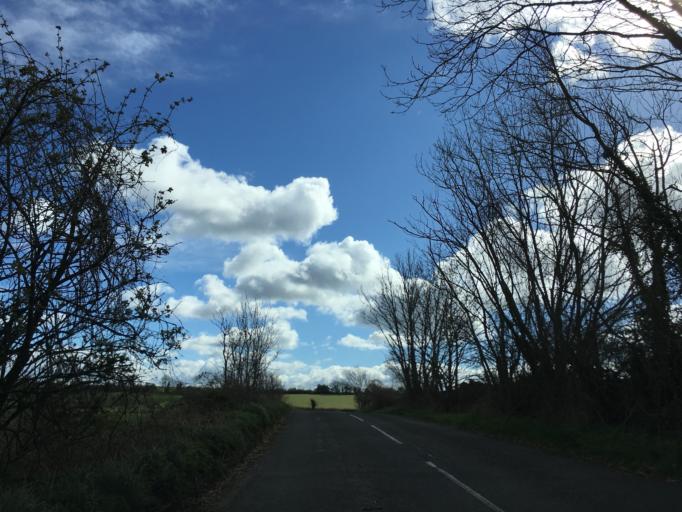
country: GB
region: England
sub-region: South Gloucestershire
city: Horton
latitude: 51.5929
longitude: -2.3346
